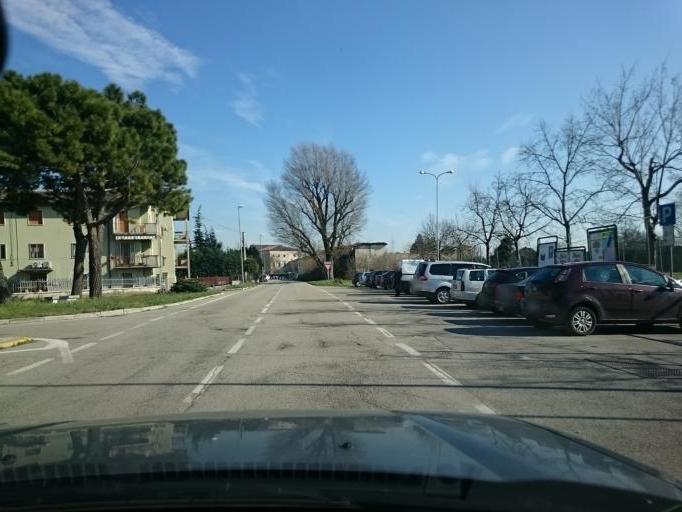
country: IT
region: Veneto
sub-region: Provincia di Verona
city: Pradelle
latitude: 45.3147
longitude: 10.8580
